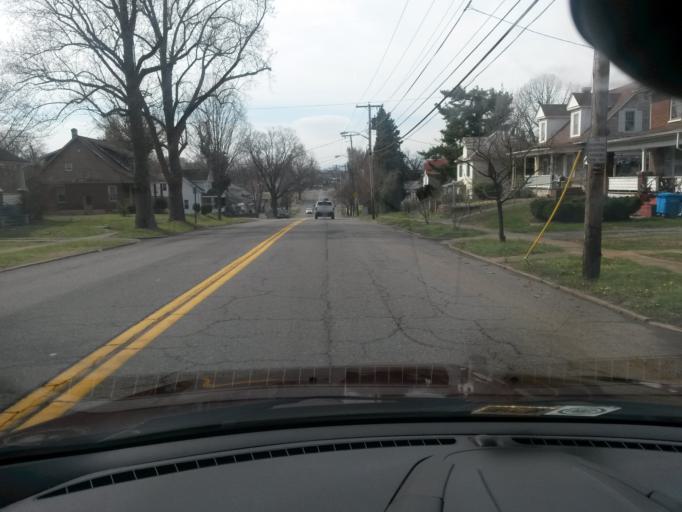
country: US
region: Virginia
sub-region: City of Roanoke
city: Roanoke
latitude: 37.2927
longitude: -79.9754
